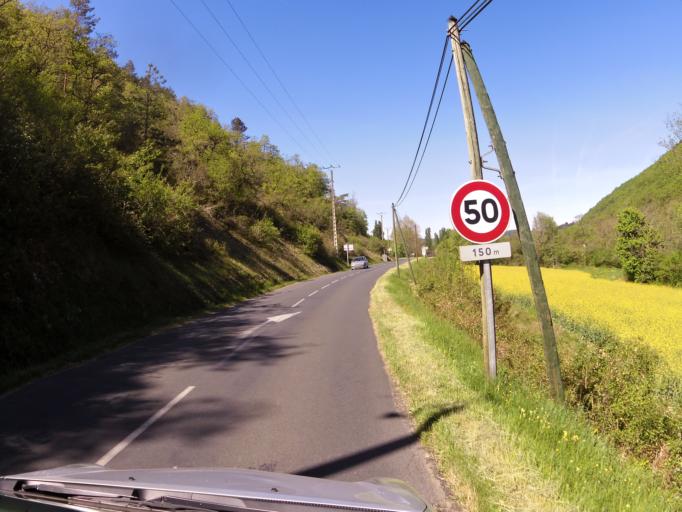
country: FR
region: Aquitaine
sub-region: Departement de la Dordogne
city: Cenac-et-Saint-Julien
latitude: 44.8072
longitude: 1.1538
